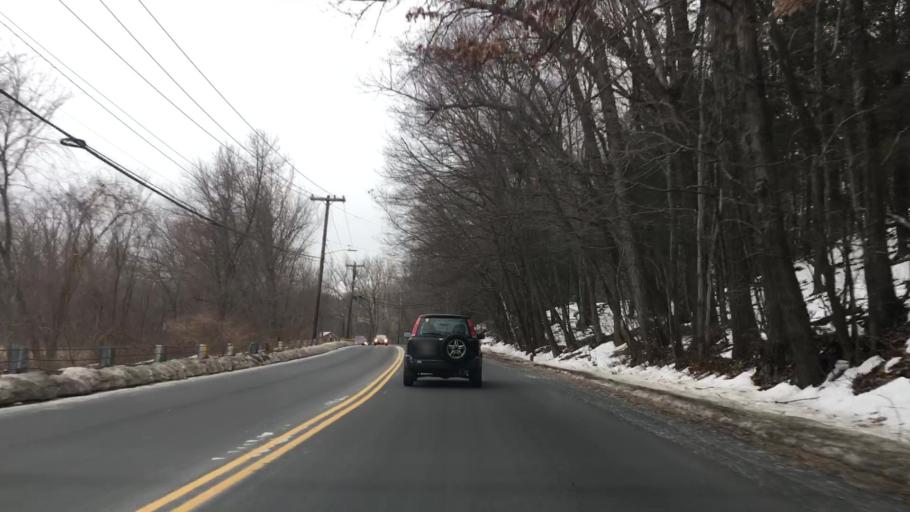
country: US
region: Massachusetts
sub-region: Hampden County
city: Westfield
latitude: 42.1159
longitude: -72.7136
